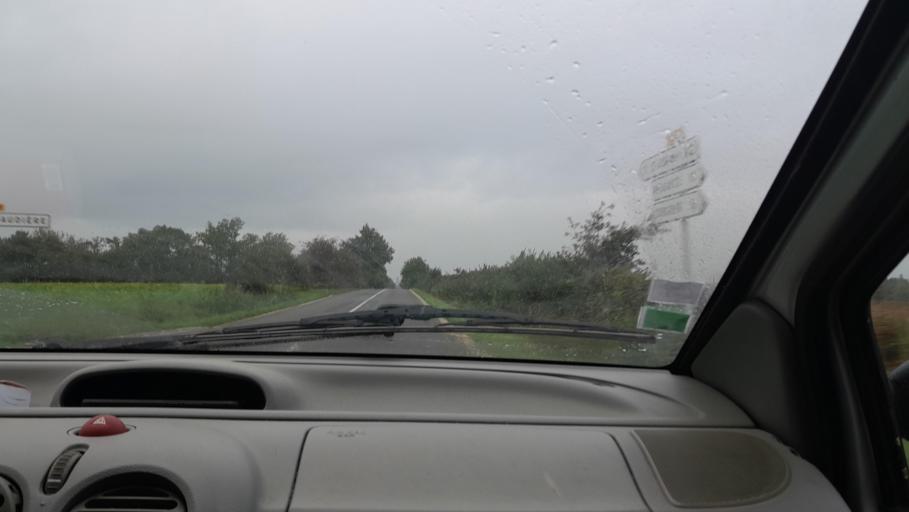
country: FR
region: Pays de la Loire
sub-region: Departement de la Mayenne
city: Congrier
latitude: 47.8255
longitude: -1.1433
